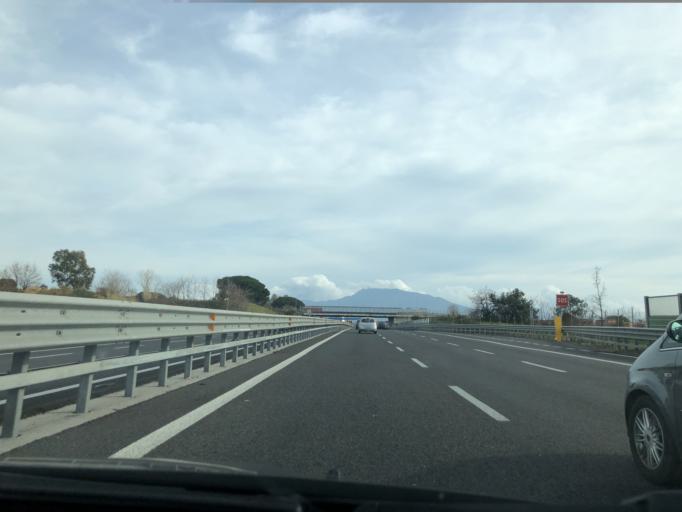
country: IT
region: Campania
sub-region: Provincia di Napoli
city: Torre del Greco
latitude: 40.7836
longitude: 14.3886
